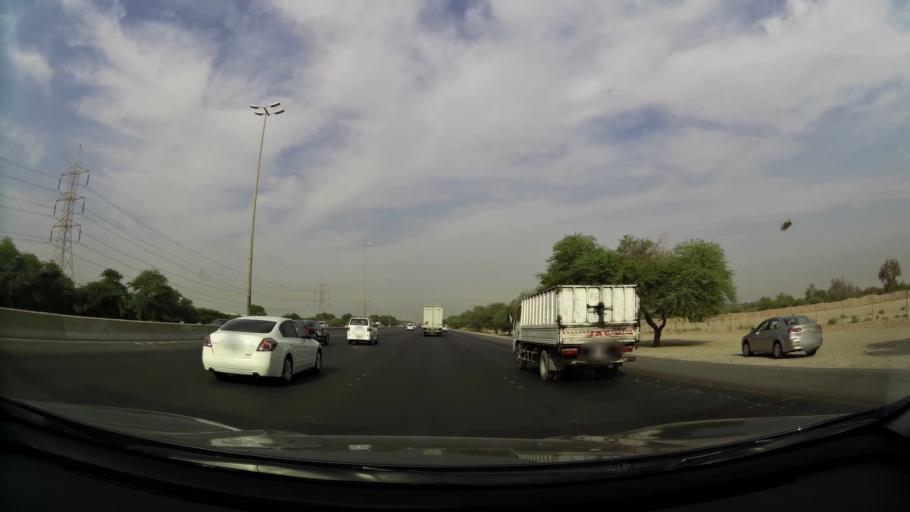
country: KW
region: Al Asimah
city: Ar Rabiyah
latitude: 29.2722
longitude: 47.8164
